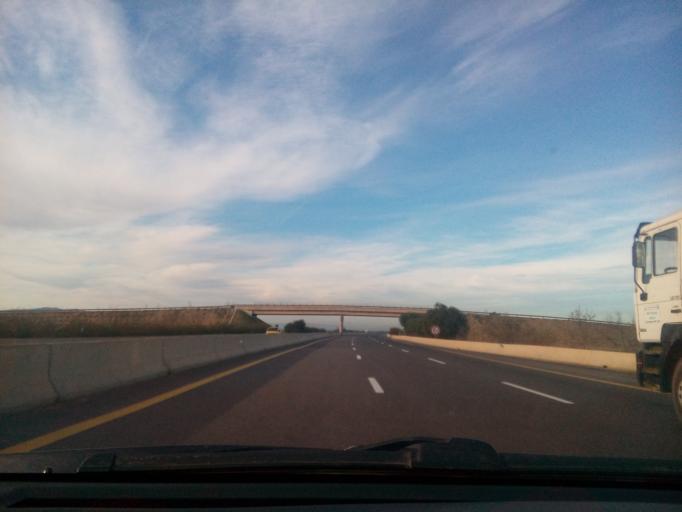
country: DZ
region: Mascara
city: Mascara
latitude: 35.6540
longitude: 0.1227
